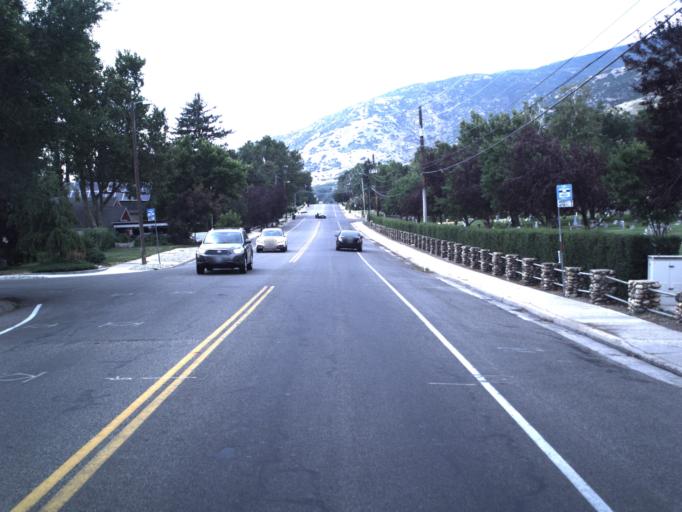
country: US
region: Utah
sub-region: Davis County
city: Farmington
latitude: 40.9707
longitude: -111.8833
